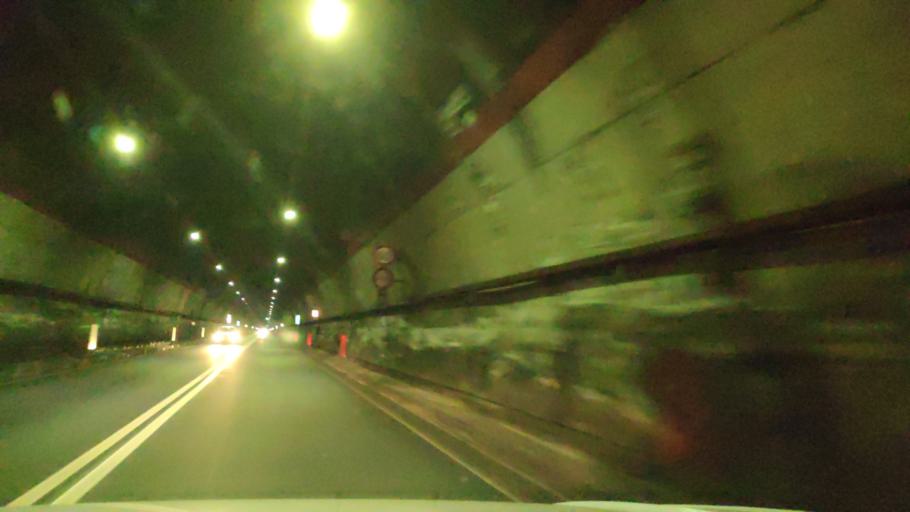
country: IT
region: Calabria
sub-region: Provincia di Reggio Calabria
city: Amato
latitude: 38.3756
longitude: 16.1769
